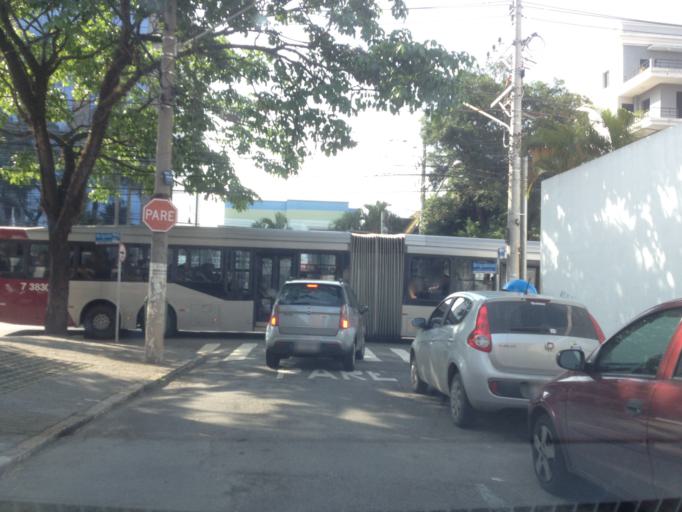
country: BR
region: Sao Paulo
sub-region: Sao Paulo
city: Sao Paulo
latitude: -23.5828
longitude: -46.6683
